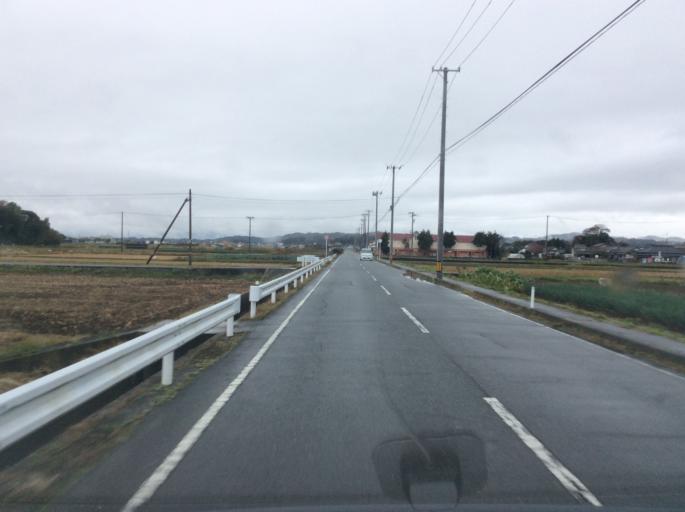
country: JP
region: Fukushima
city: Iwaki
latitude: 37.0674
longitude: 140.9637
